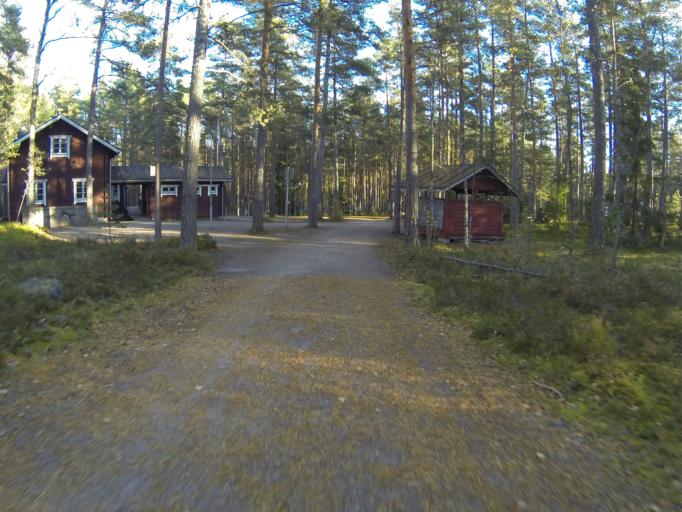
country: FI
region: Varsinais-Suomi
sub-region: Salo
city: Saerkisalo
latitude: 60.2101
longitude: 22.9355
